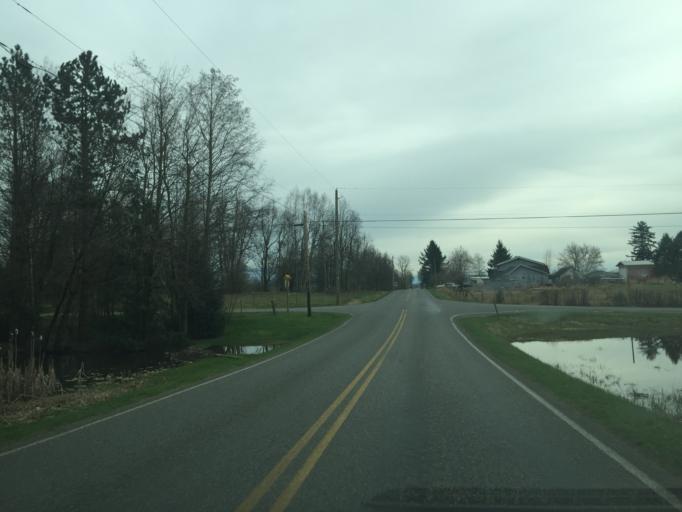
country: US
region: Washington
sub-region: Whatcom County
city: Everson
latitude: 48.9495
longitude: -122.3524
